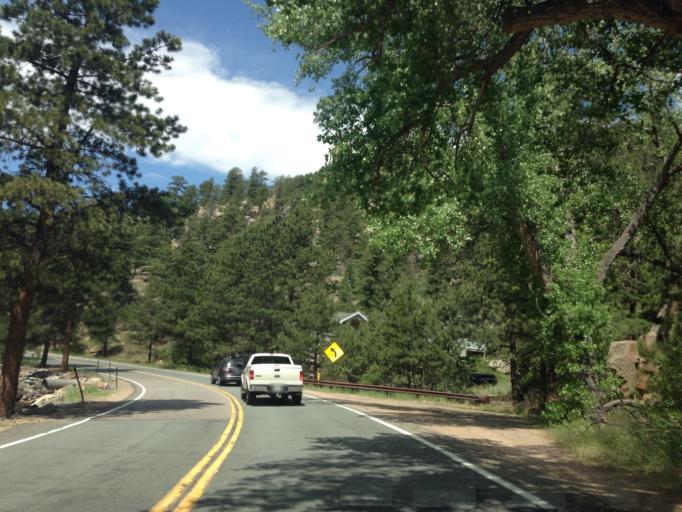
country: US
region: Colorado
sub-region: Larimer County
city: Estes Park
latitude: 40.3940
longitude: -105.4472
